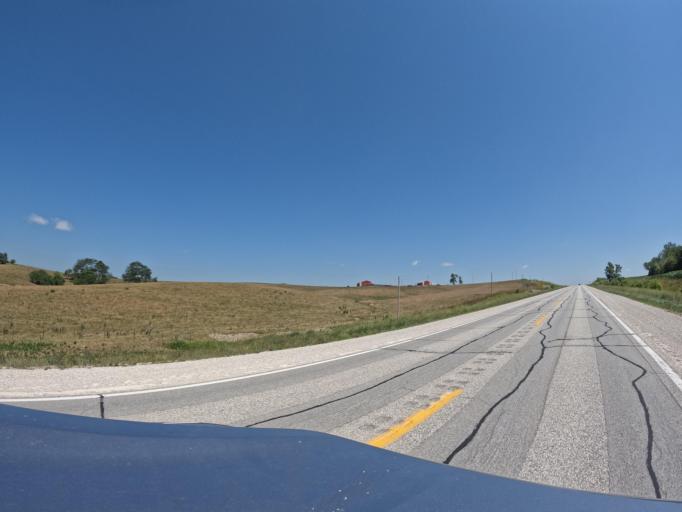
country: US
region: Iowa
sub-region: Keokuk County
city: Sigourney
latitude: 41.2431
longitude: -92.2109
